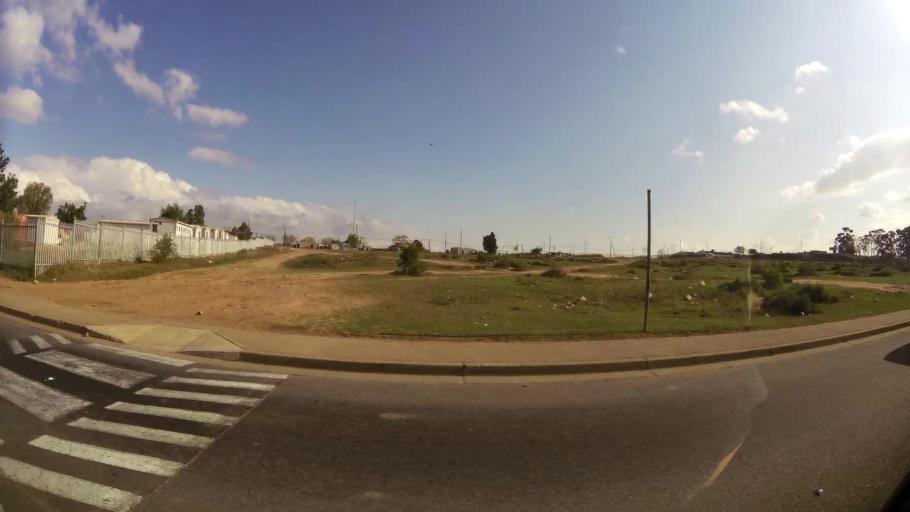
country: ZA
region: Eastern Cape
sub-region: Nelson Mandela Bay Metropolitan Municipality
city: Uitenhage
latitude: -33.7525
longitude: 25.3856
